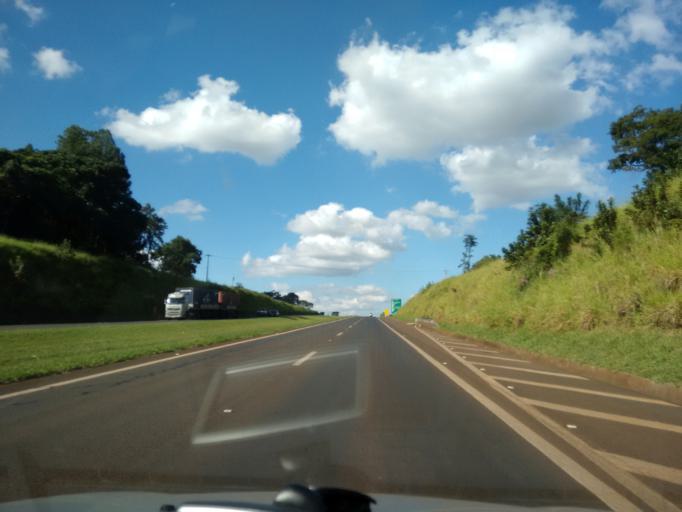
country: BR
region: Sao Paulo
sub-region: Araraquara
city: Araraquara
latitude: -21.8143
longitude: -48.1650
